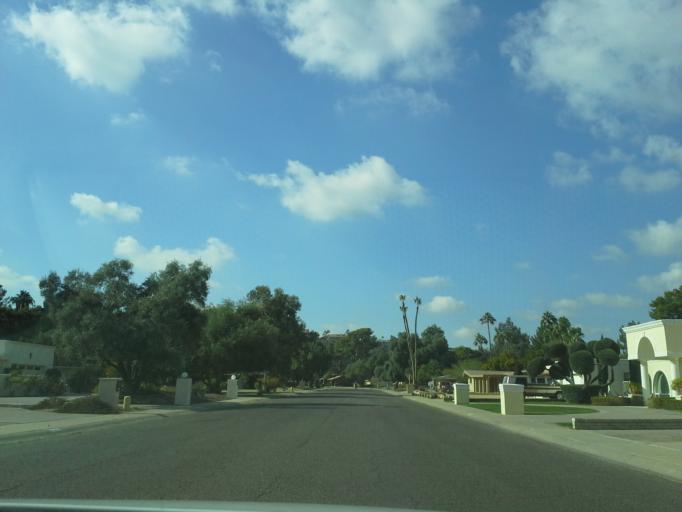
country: US
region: Arizona
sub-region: Maricopa County
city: Glendale
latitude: 33.6200
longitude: -112.0814
